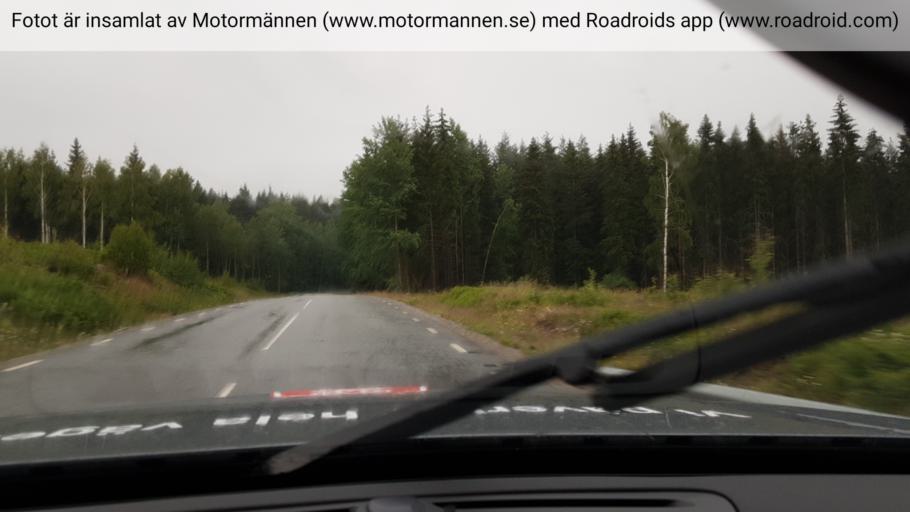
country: SE
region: Vaestmanland
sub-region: Norbergs Kommun
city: Norberg
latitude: 59.9947
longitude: 16.0696
